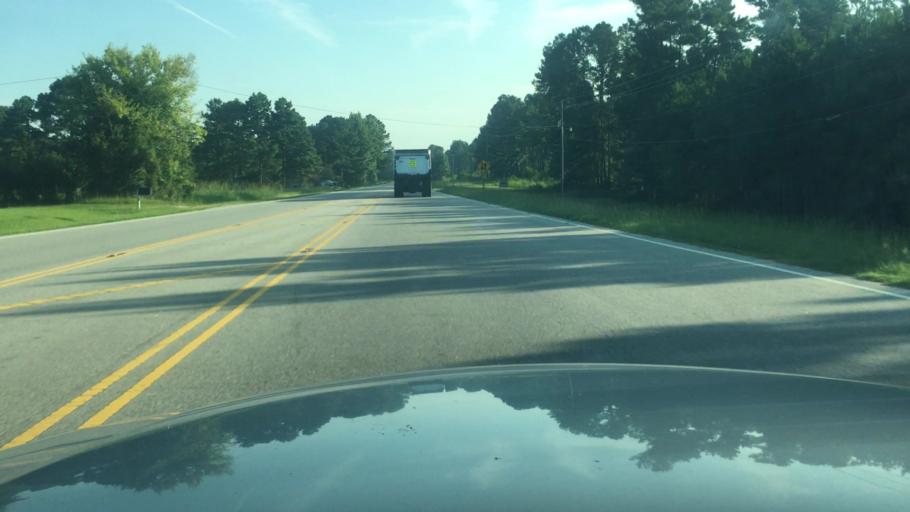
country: US
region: North Carolina
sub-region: Cumberland County
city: Eastover
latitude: 35.1852
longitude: -78.8528
